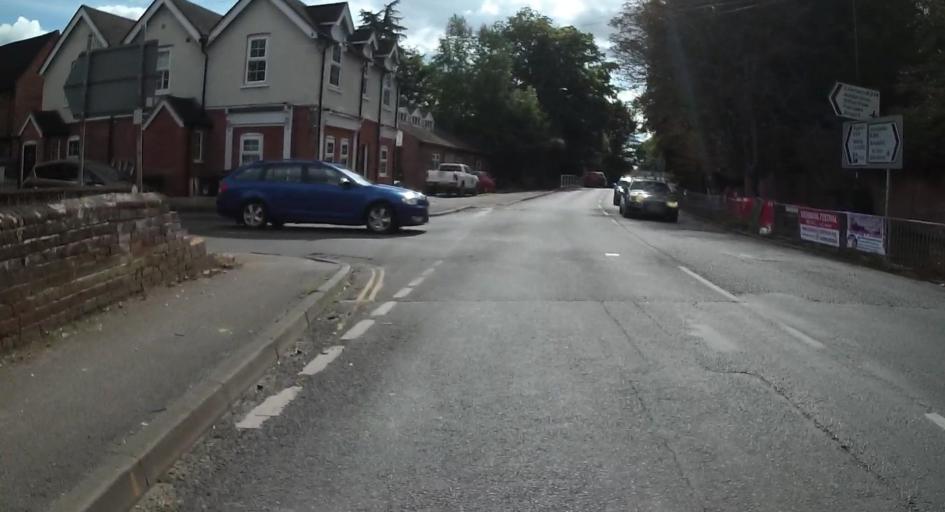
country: GB
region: England
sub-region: Surrey
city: Chobham
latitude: 51.3498
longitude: -0.6030
